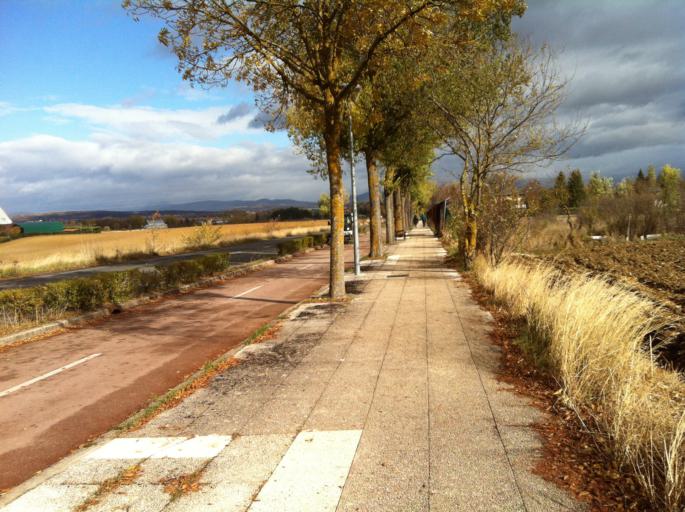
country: ES
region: Basque Country
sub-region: Provincia de Alava
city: Gasteiz / Vitoria
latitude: 42.8268
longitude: -2.6943
